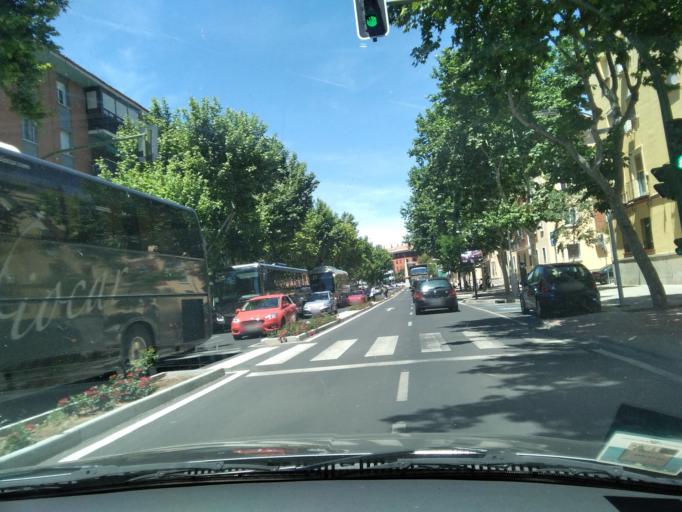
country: ES
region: Castille-La Mancha
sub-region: Province of Toledo
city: Toledo
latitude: 39.8664
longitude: -4.0288
